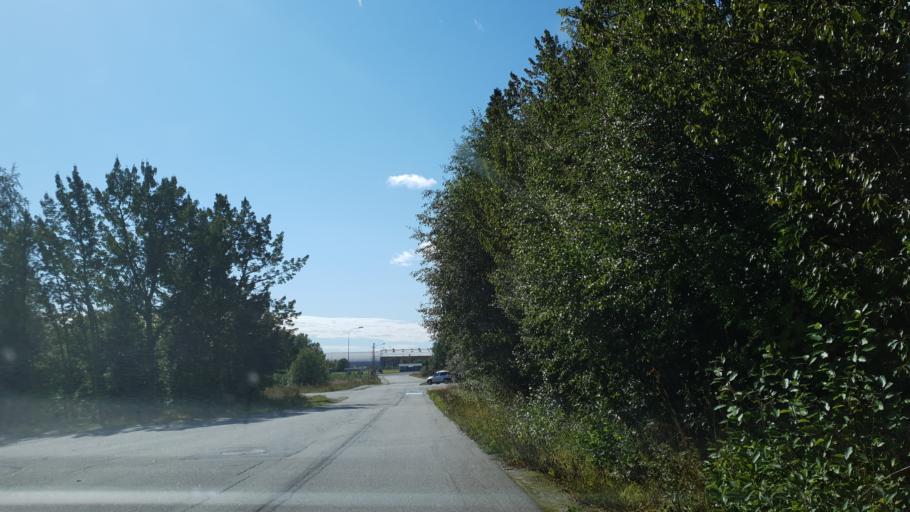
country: SE
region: Vaesterbotten
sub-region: Umea Kommun
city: Holmsund
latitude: 63.7046
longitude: 20.3550
